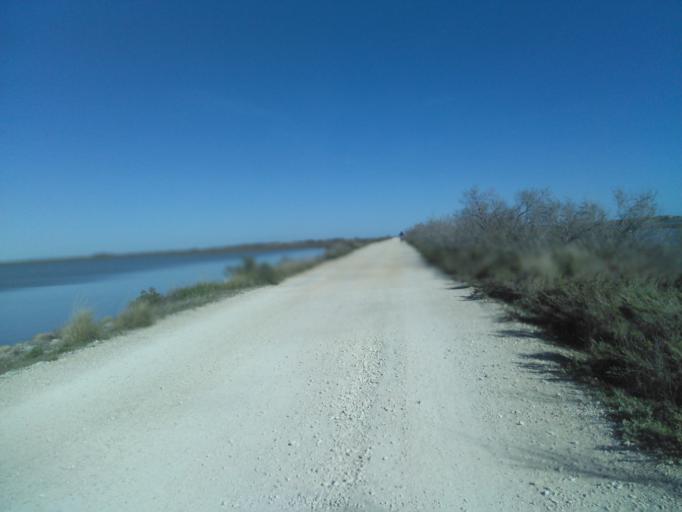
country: FR
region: Provence-Alpes-Cote d'Azur
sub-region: Departement des Bouches-du-Rhone
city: Saintes-Maries-de-la-Mer
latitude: 43.4616
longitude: 4.4834
